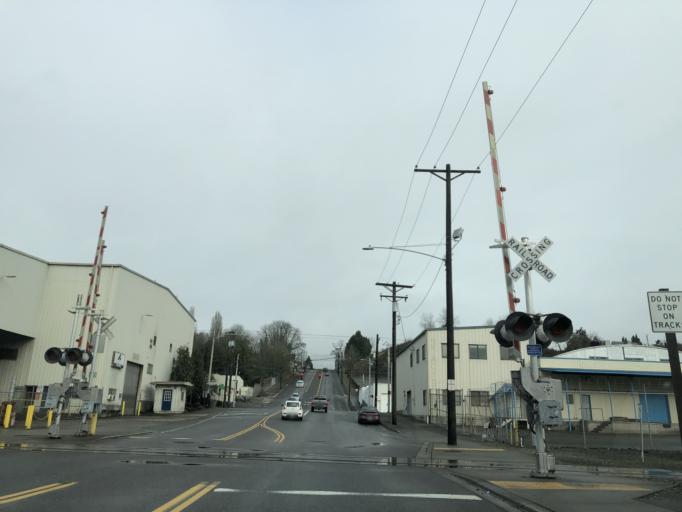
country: US
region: Washington
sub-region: Pierce County
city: Tacoma
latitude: 47.2329
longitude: -122.4589
